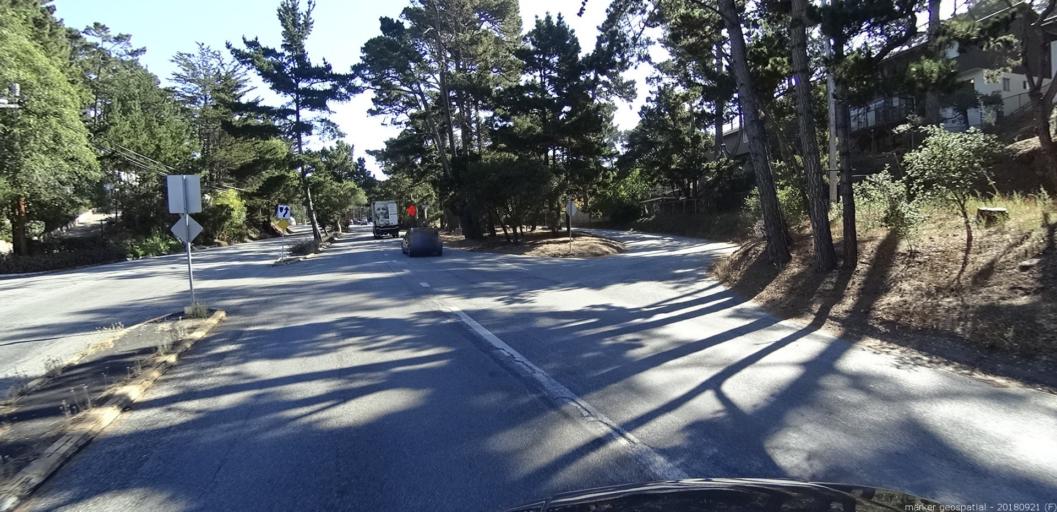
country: US
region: California
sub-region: Monterey County
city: Carmel-by-the-Sea
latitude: 36.5656
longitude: -121.9148
